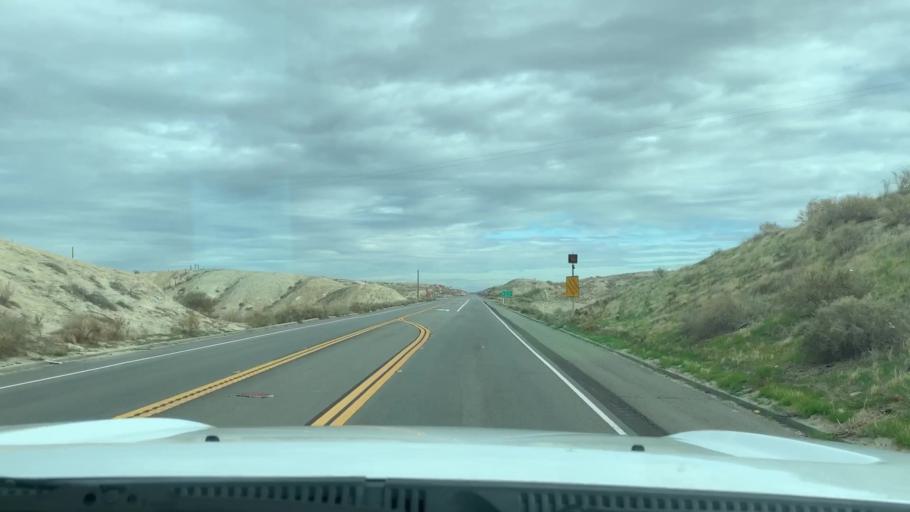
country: US
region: California
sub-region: Kern County
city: Ford City
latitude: 35.2377
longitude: -119.3617
